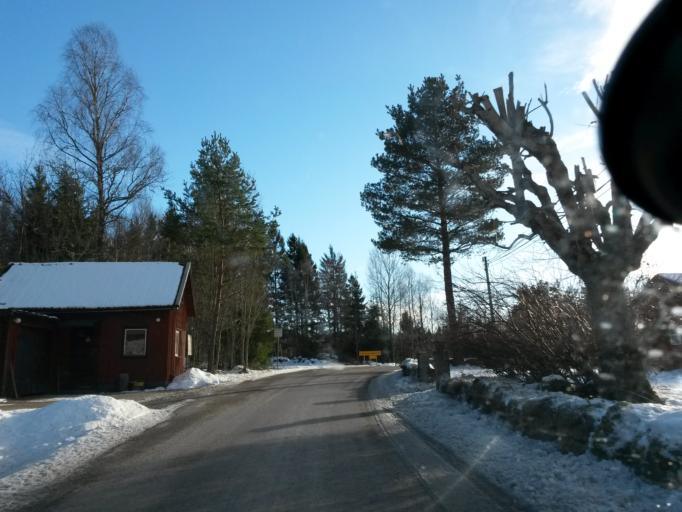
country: SE
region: Vaestra Goetaland
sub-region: Vargarda Kommun
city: Vargarda
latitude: 58.0144
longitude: 12.8923
